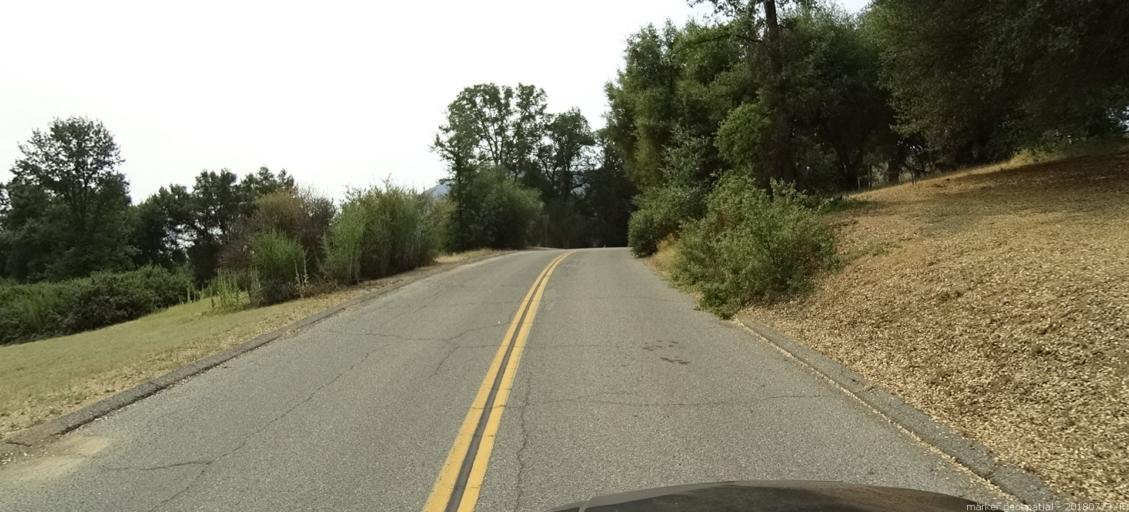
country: US
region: California
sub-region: Madera County
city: Ahwahnee
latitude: 37.3389
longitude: -119.7116
